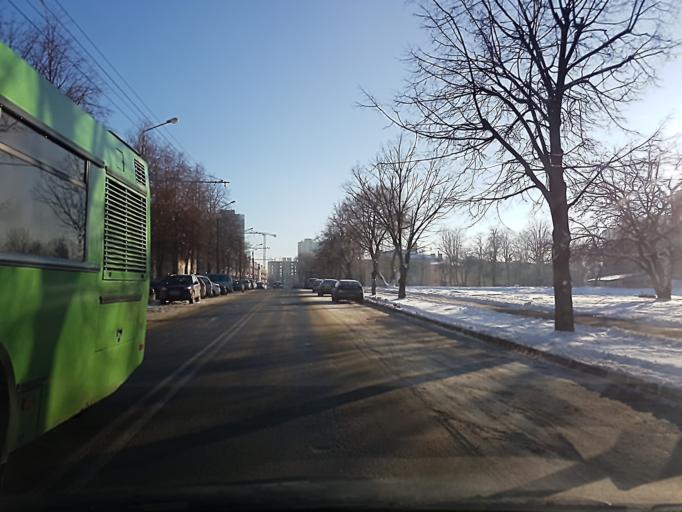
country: BY
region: Minsk
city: Minsk
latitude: 53.8919
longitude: 27.5140
